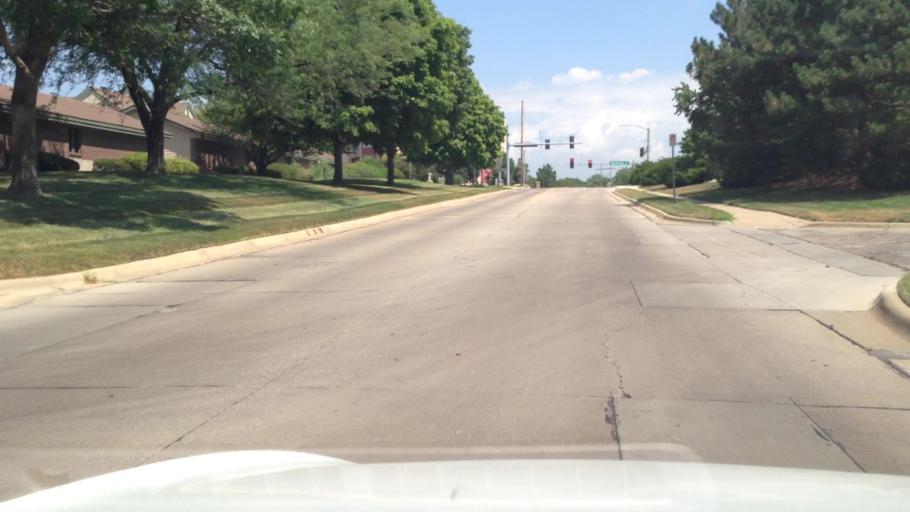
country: US
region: Kansas
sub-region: Douglas County
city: Lawrence
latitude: 38.9557
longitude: -95.3022
